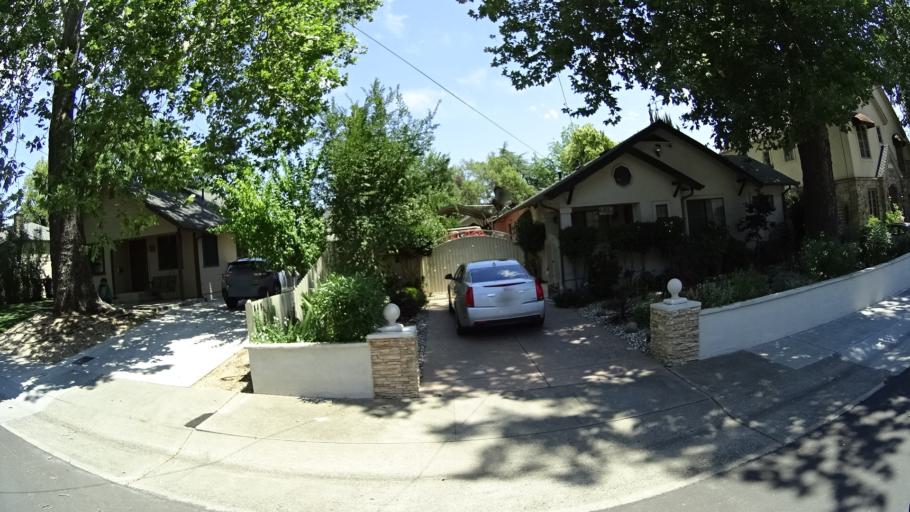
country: US
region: California
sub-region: Sacramento County
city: Sacramento
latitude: 38.5687
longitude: -121.4438
